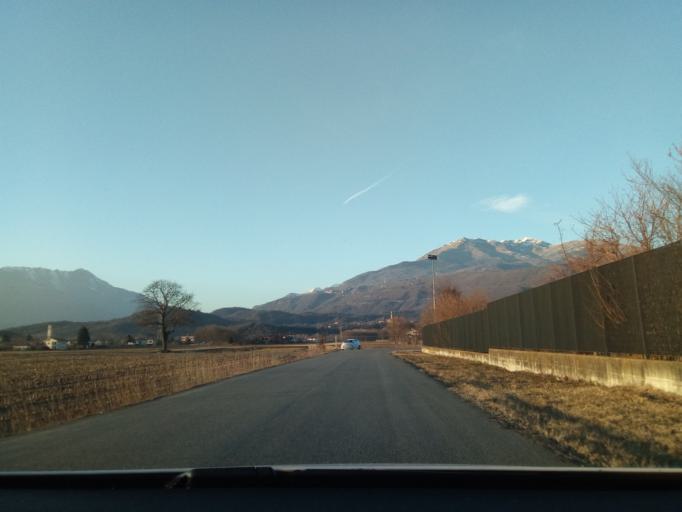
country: IT
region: Piedmont
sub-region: Provincia di Torino
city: Cascinette d'Ivrea
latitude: 45.4741
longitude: 7.9165
